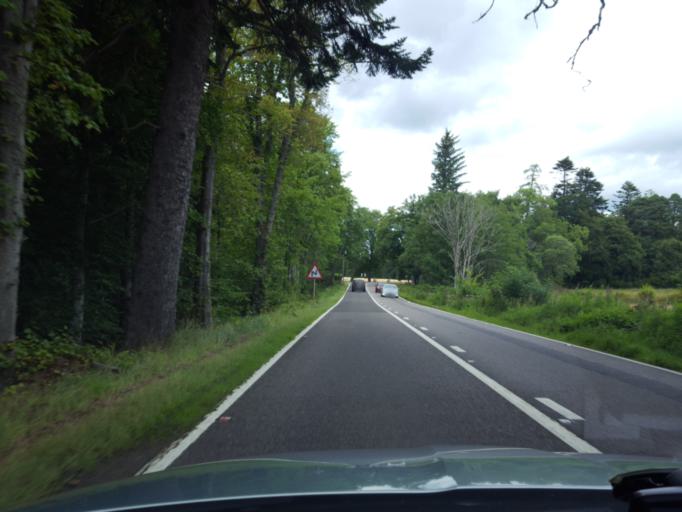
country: GB
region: Scotland
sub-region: Moray
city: Rothes
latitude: 57.4097
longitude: -3.3579
